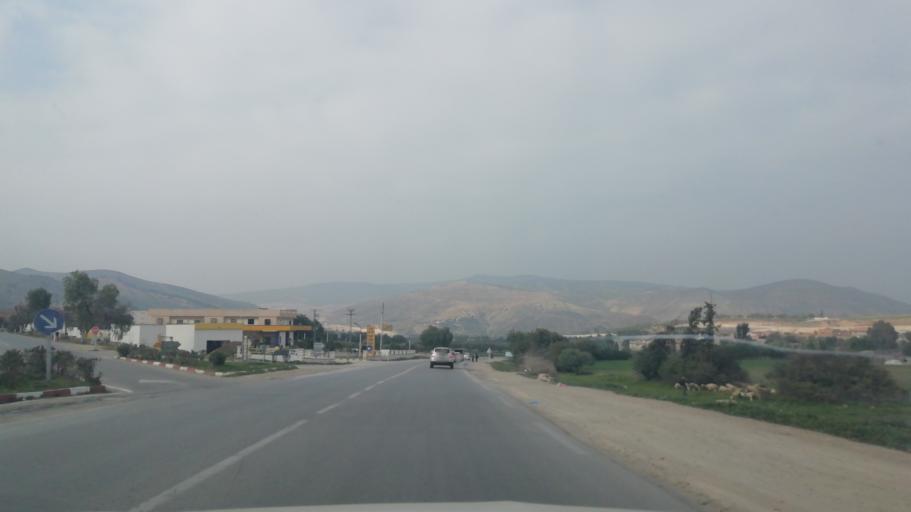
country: DZ
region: Mascara
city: Mascara
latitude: 35.4576
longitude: 0.0022
